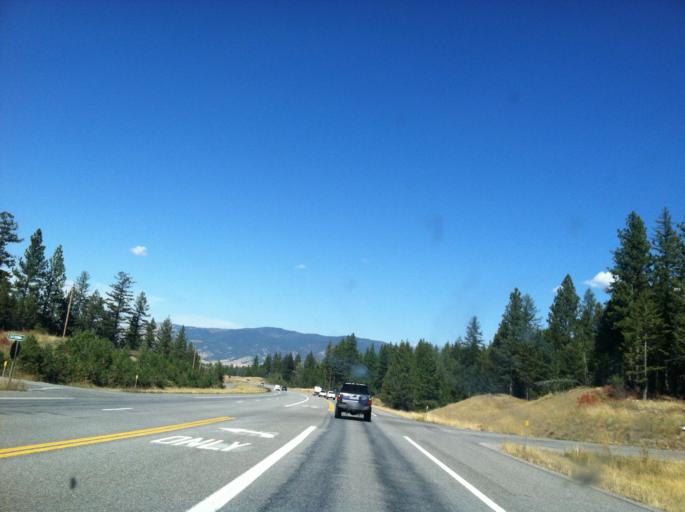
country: US
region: Montana
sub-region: Missoula County
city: Frenchtown
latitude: 47.0881
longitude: -114.0410
